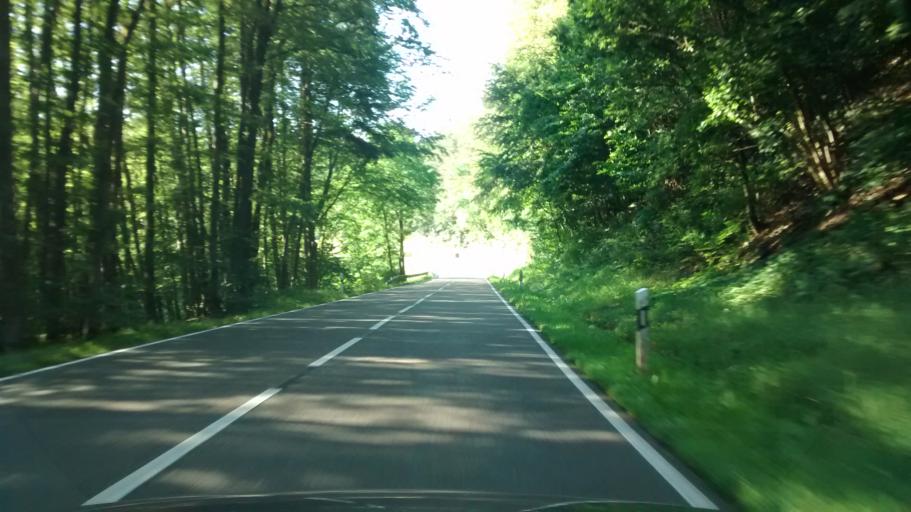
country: DE
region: Rheinland-Pfalz
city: Vorderweidenthal
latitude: 49.1271
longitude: 7.8954
